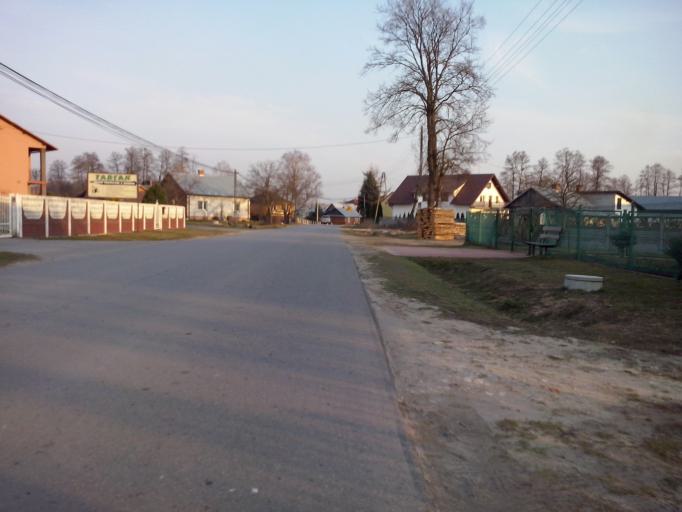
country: PL
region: Subcarpathian Voivodeship
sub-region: Powiat nizanski
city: Krzeszow
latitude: 50.3967
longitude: 22.3577
